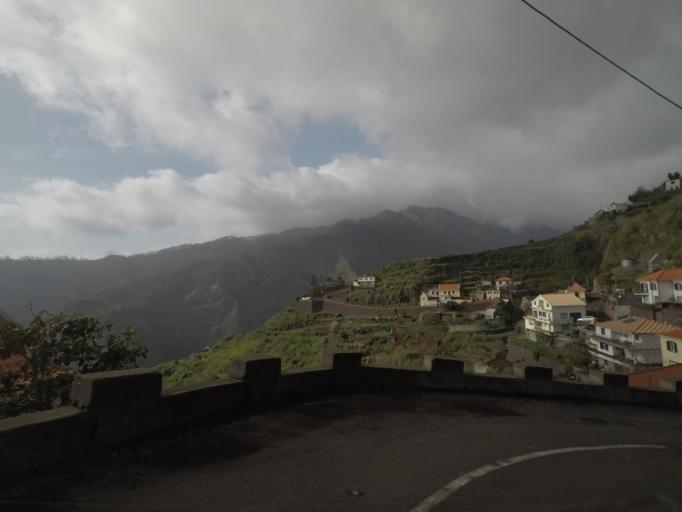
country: PT
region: Madeira
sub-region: Ribeira Brava
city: Campanario
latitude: 32.7059
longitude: -17.0295
